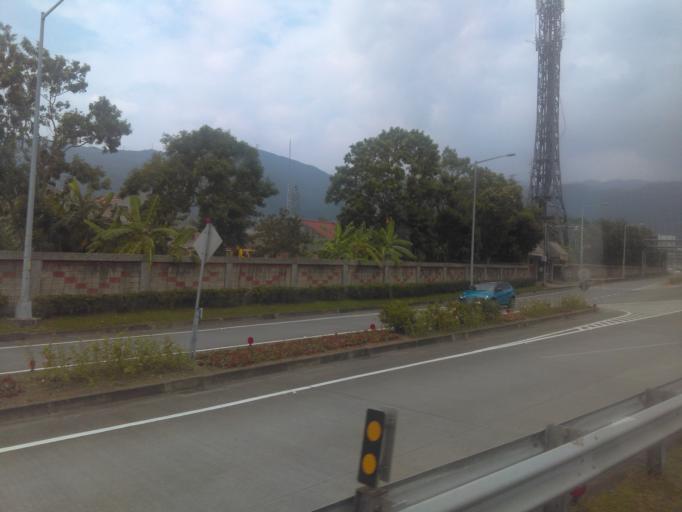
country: TW
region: Taiwan
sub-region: Yilan
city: Yilan
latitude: 24.8294
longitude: 121.7923
